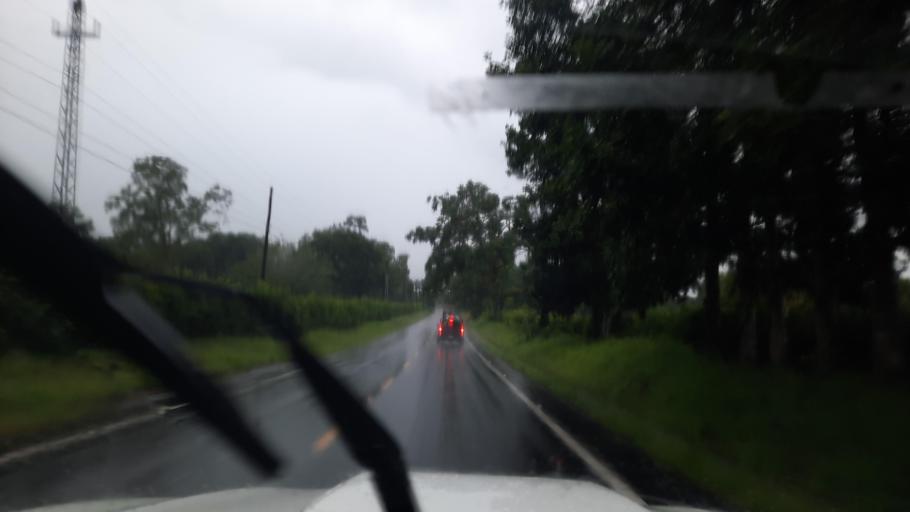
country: PA
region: Chiriqui
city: Sortova
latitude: 8.5661
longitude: -82.6307
